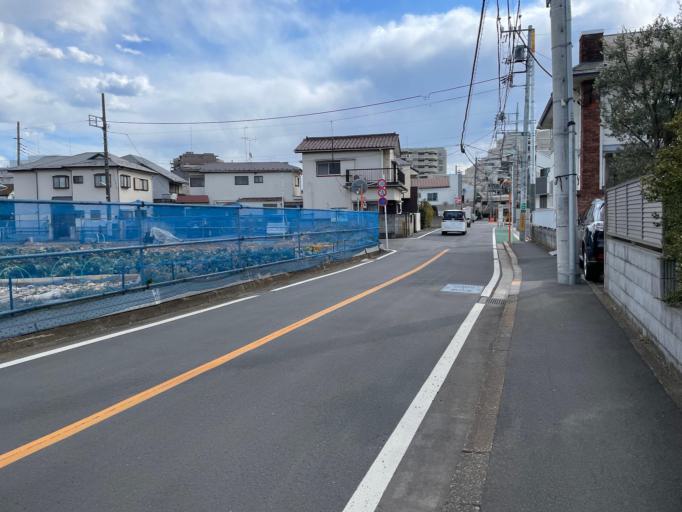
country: JP
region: Tokyo
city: Chofugaoka
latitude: 35.6524
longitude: 139.5227
